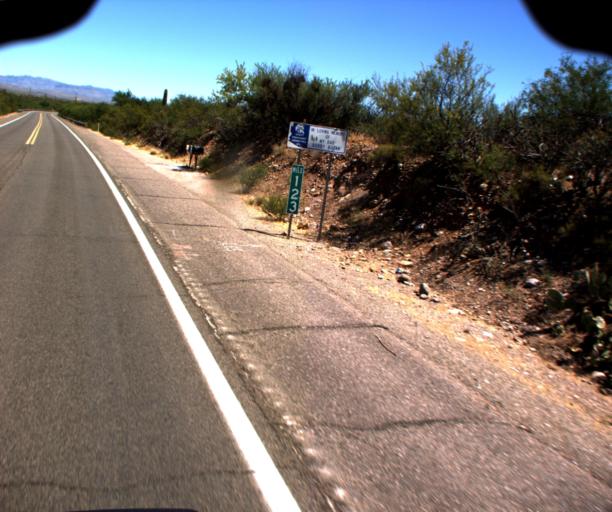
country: US
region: Arizona
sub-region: Pinal County
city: Mammoth
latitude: 32.8327
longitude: -110.7053
